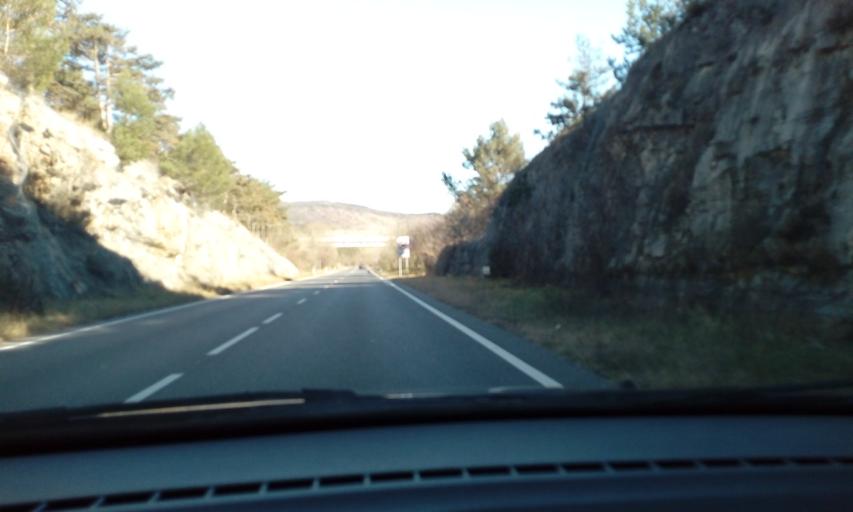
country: IT
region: Friuli Venezia Giulia
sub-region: Provincia di Gorizia
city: Monfalcone
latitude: 45.7993
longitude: 13.5759
